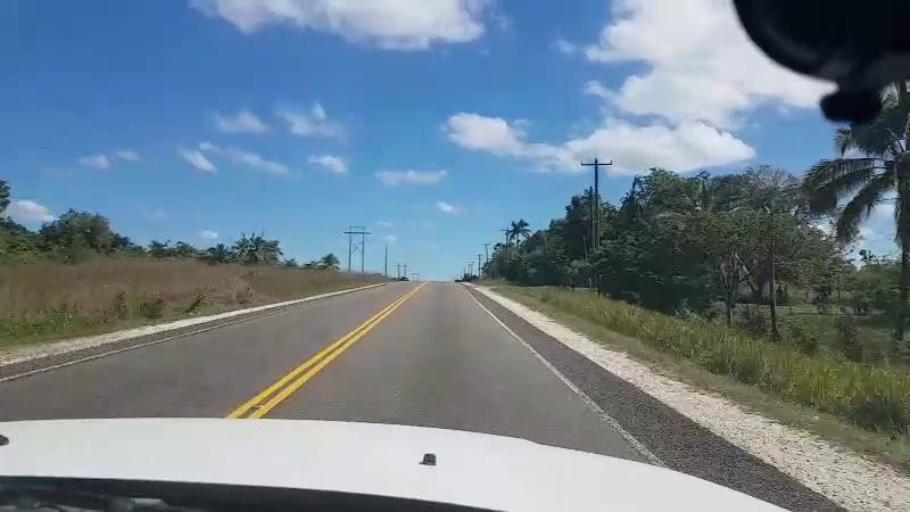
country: BZ
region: Cayo
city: Belmopan
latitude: 17.2771
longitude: -88.6563
